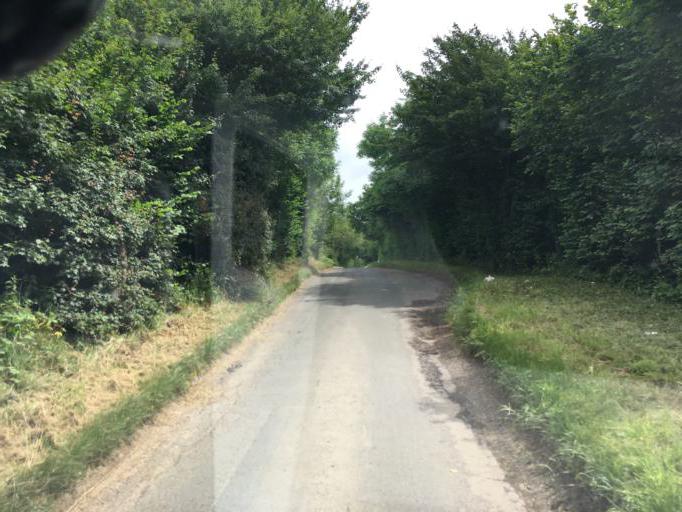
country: GB
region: England
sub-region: Gloucestershire
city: Stonehouse
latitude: 51.7030
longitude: -2.2692
